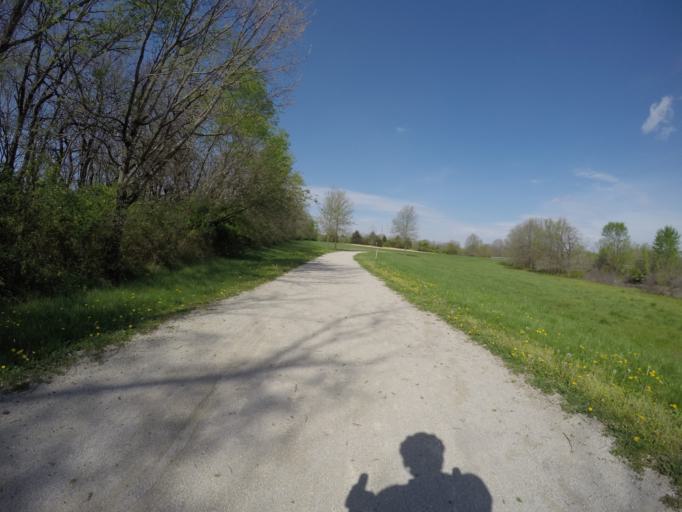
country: US
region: Missouri
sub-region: Jackson County
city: Grandview
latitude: 38.9071
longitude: -94.4809
